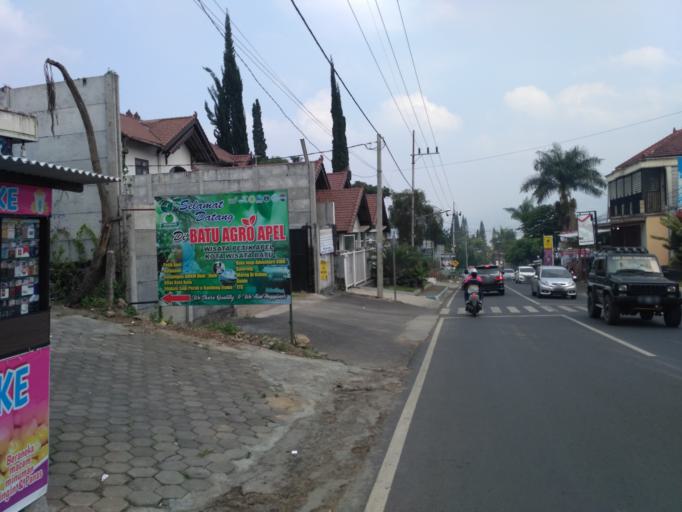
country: ID
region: East Java
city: Batu
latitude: -7.8387
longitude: 112.5283
